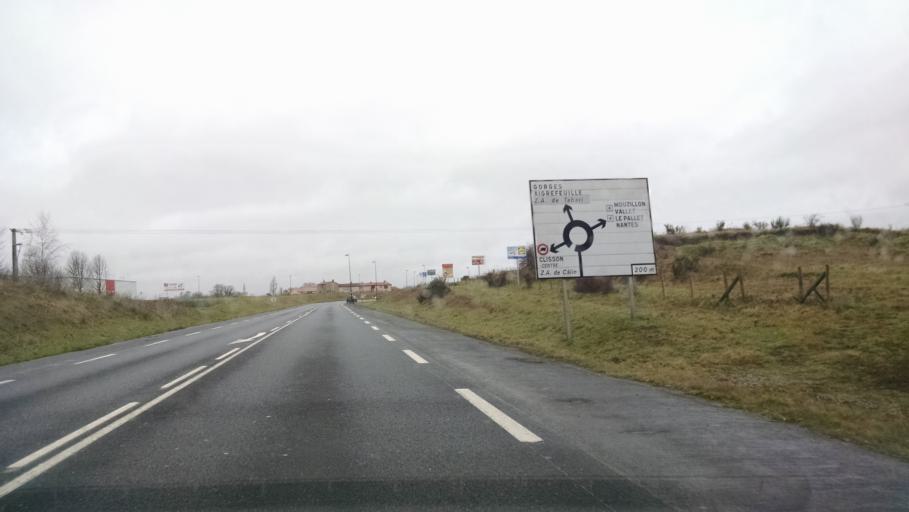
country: FR
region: Pays de la Loire
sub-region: Departement de la Loire-Atlantique
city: Clisson
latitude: 47.0996
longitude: -1.2789
